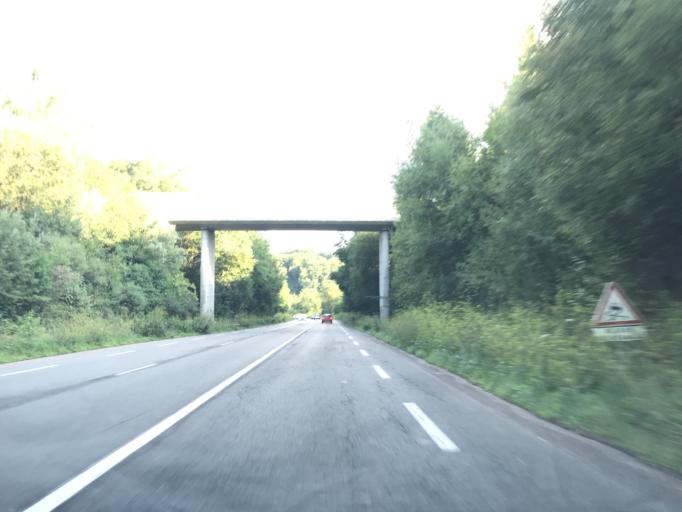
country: FR
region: Haute-Normandie
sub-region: Departement de la Seine-Maritime
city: Bolbec
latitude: 49.5676
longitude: 0.4642
